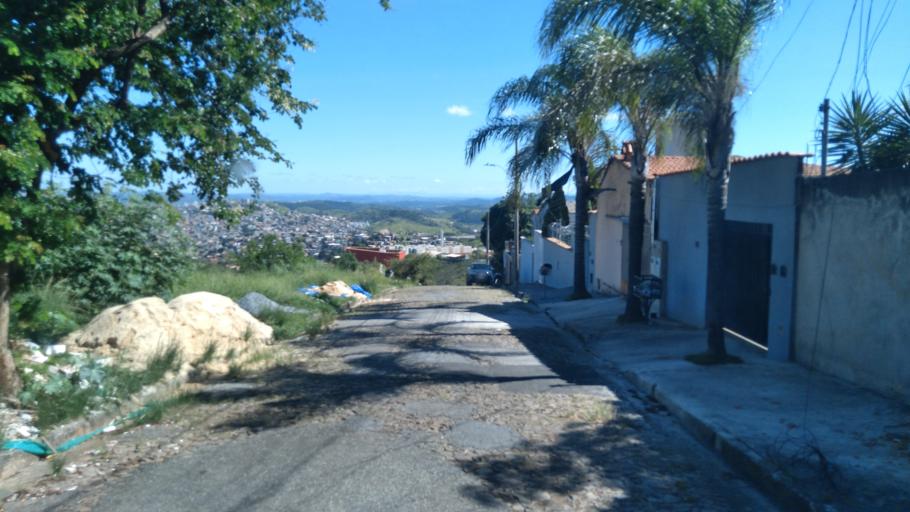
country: BR
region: Minas Gerais
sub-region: Belo Horizonte
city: Belo Horizonte
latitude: -19.9253
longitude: -43.8915
